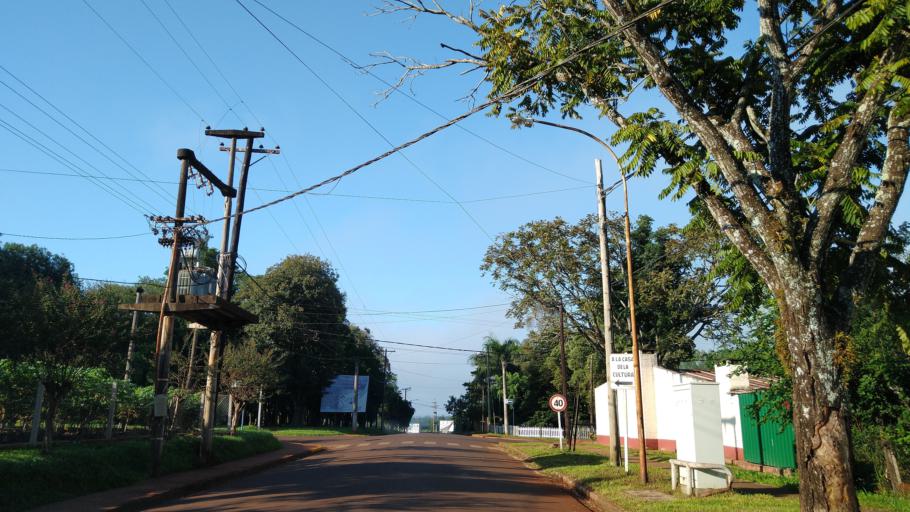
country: AR
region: Misiones
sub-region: Departamento de Montecarlo
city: Montecarlo
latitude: -26.5674
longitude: -54.7732
